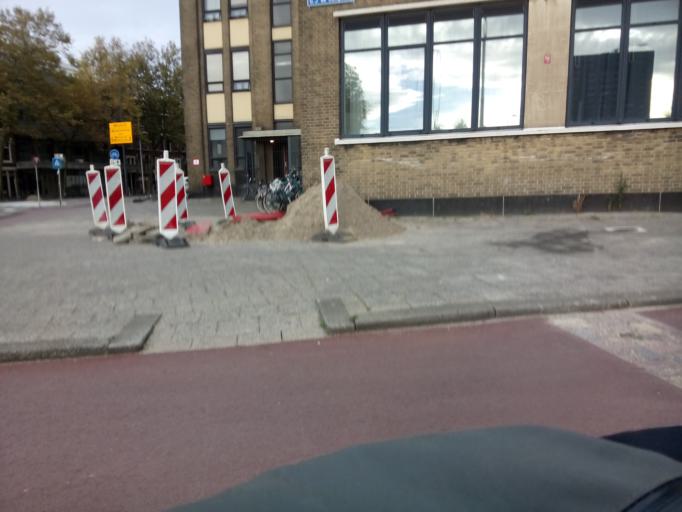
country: NL
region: South Holland
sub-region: Gemeente Rotterdam
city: Delfshaven
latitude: 51.9103
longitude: 4.4602
